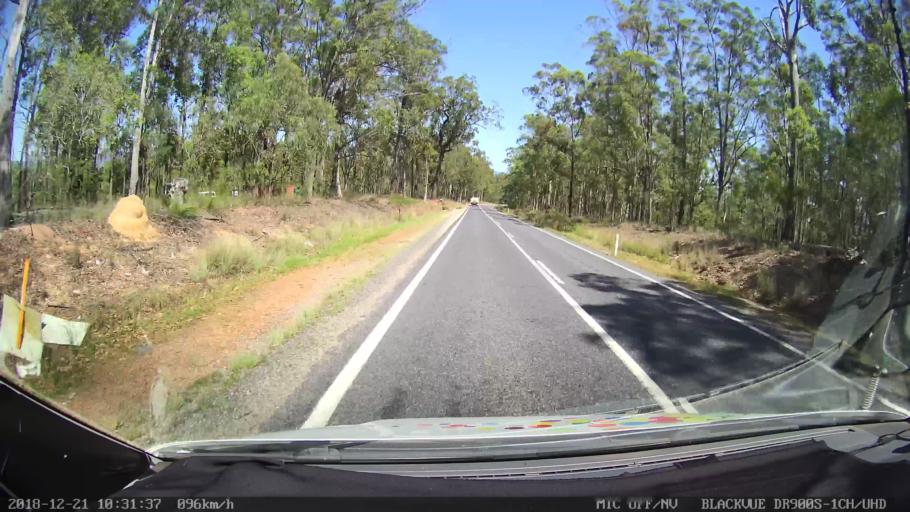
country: AU
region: New South Wales
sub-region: Clarence Valley
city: South Grafton
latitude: -29.6296
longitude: 152.6937
